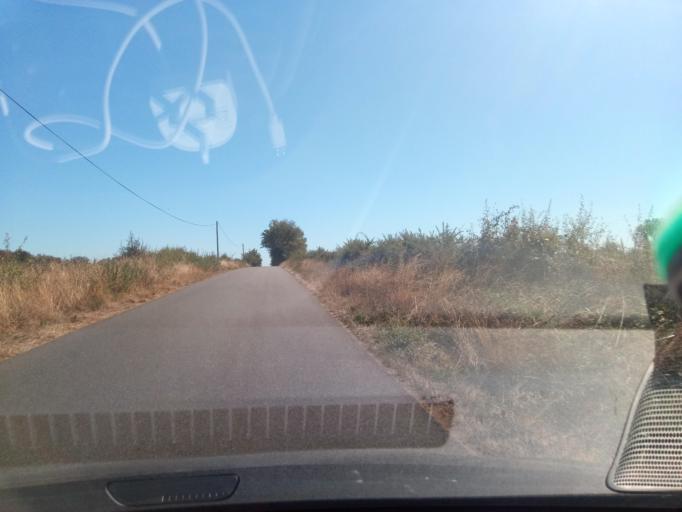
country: FR
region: Poitou-Charentes
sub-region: Departement de la Vienne
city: Saulge
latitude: 46.3790
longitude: 0.8966
